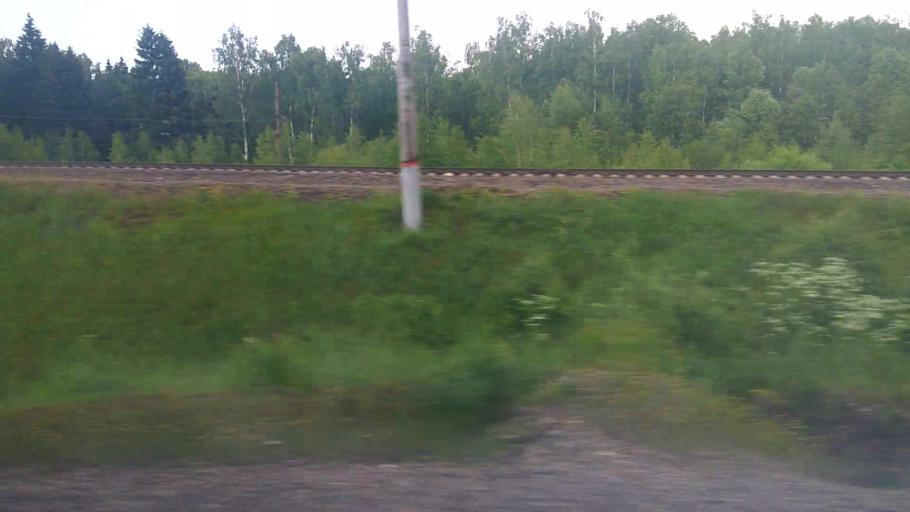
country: RU
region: Moskovskaya
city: Zhilevo
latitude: 54.9991
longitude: 38.0243
